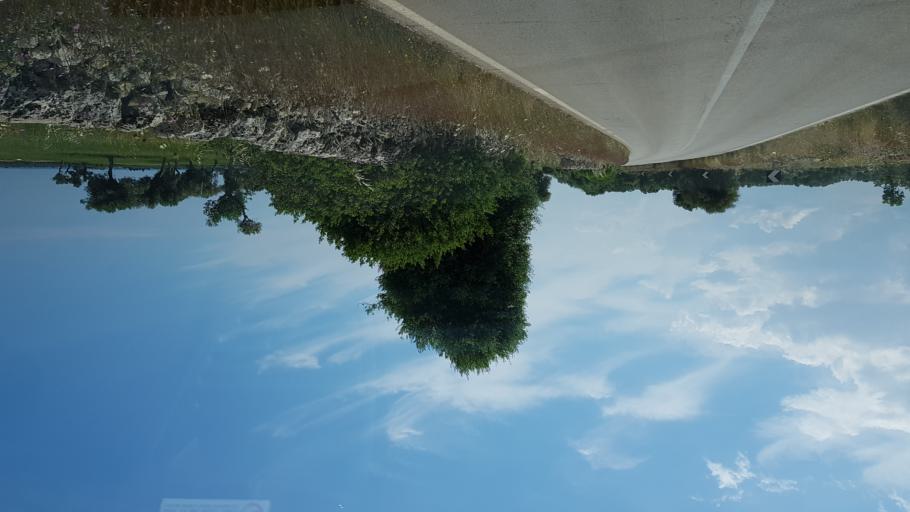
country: IT
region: Apulia
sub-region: Provincia di Lecce
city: Porto Cesareo
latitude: 40.3182
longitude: 17.8598
